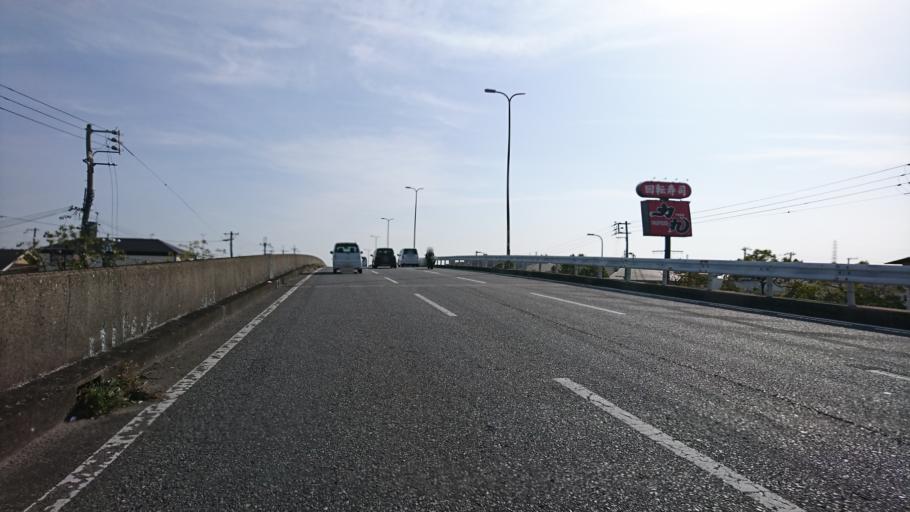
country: JP
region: Hyogo
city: Kakogawacho-honmachi
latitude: 34.7402
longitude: 134.8459
